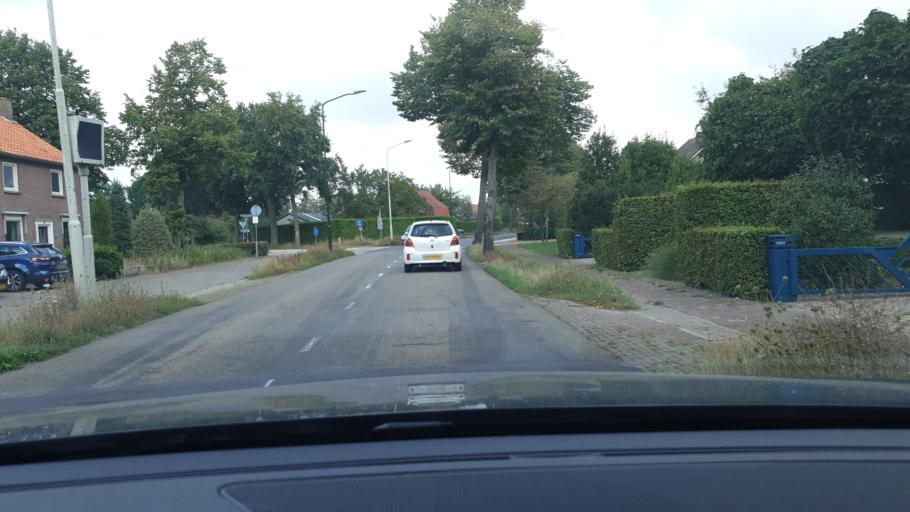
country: NL
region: North Brabant
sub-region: Gemeente Oirschot
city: Oostelbeers
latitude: 51.4742
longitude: 5.2694
